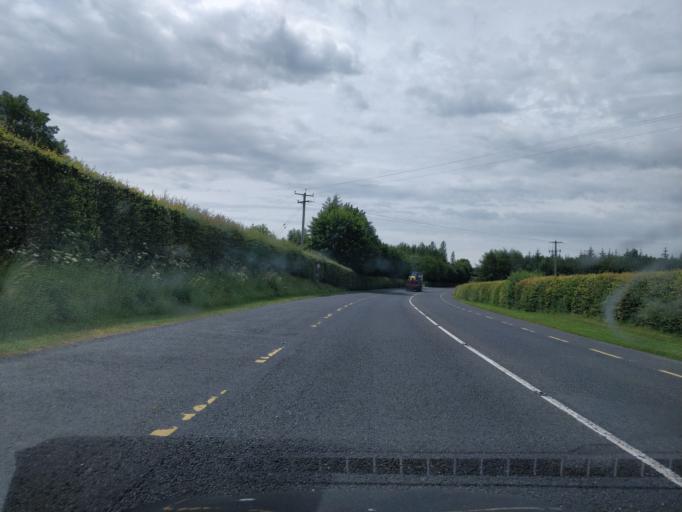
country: IE
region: Leinster
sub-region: Laois
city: Mountrath
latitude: 52.9811
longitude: -7.4930
